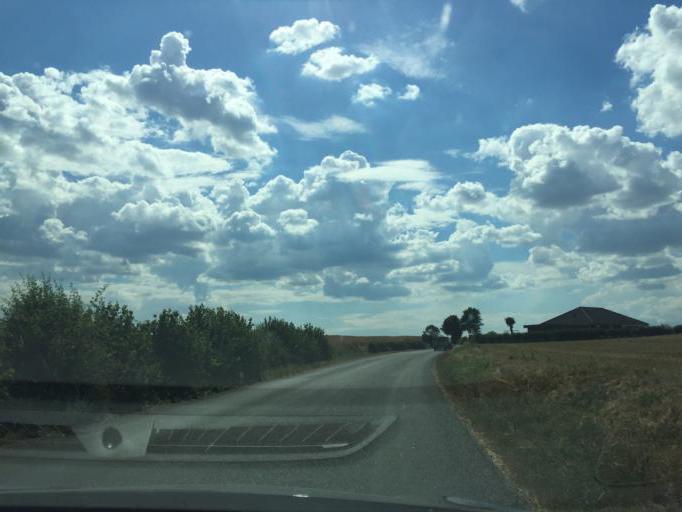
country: DK
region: South Denmark
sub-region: Odense Kommune
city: Bellinge
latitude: 55.2388
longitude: 10.2775
